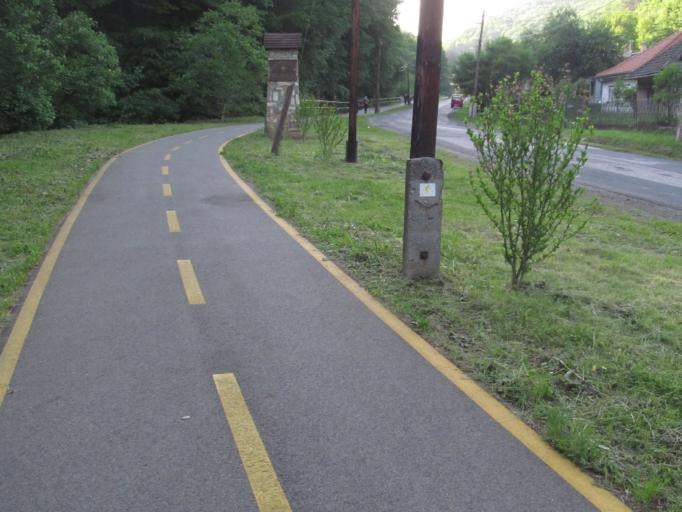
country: HU
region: Borsod-Abauj-Zemplen
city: Gonc
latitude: 48.5281
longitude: 21.4289
